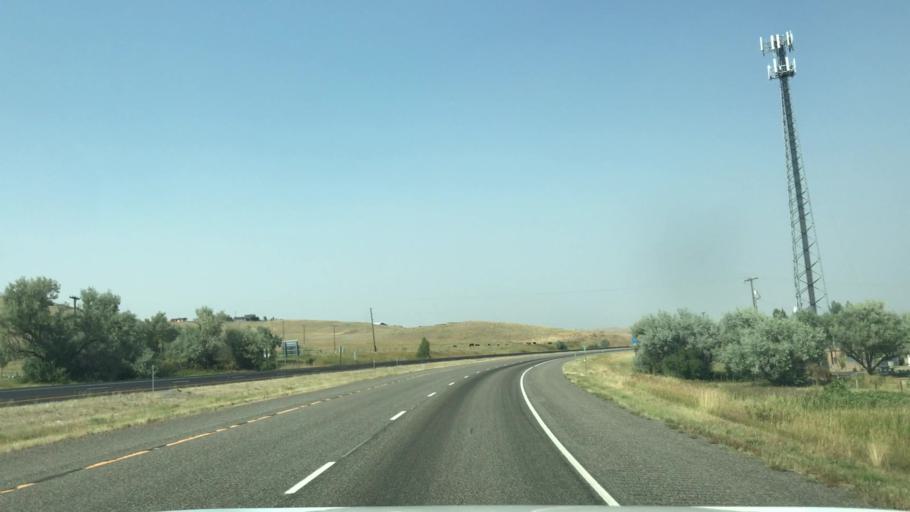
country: US
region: Montana
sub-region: Cascade County
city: Sun Prairie
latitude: 47.2740
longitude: -111.7073
